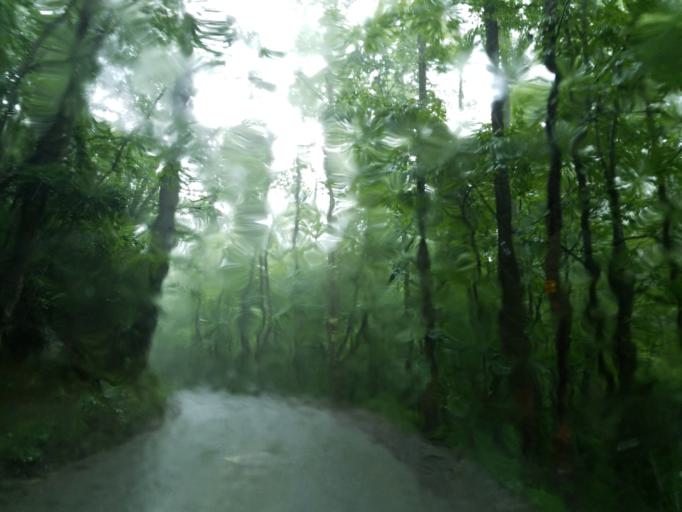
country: US
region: Georgia
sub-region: Fannin County
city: Blue Ridge
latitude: 34.7813
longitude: -84.3072
